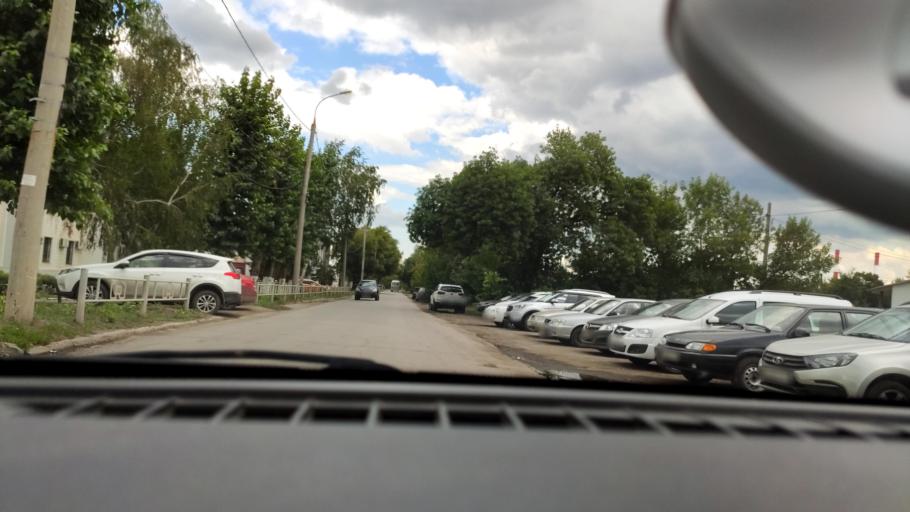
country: RU
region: Samara
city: Novokuybyshevsk
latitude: 53.1047
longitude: 50.0383
